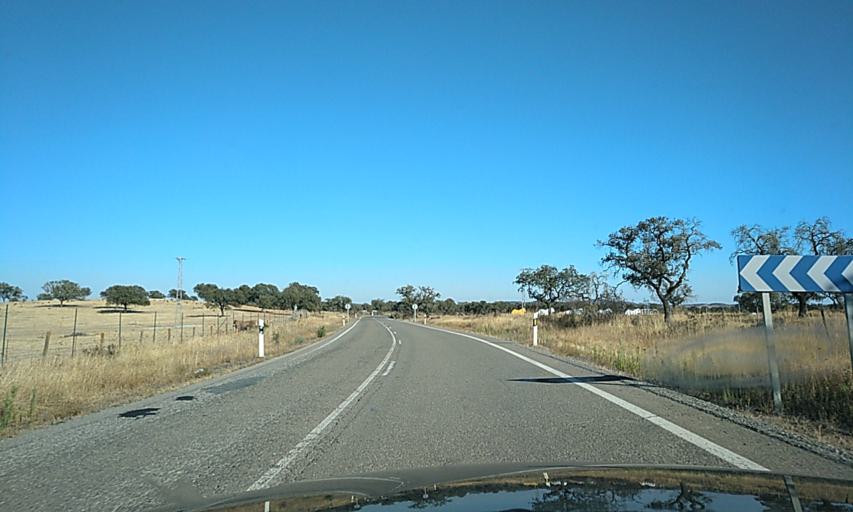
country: ES
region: Andalusia
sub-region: Provincia de Huelva
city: Santa Barbara de Casa
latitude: 37.7724
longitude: -7.1459
